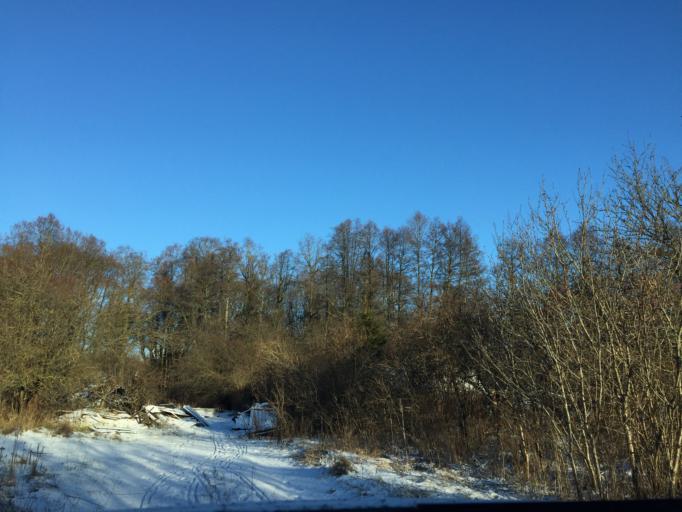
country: LV
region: Kekava
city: Balozi
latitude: 56.9097
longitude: 24.1361
